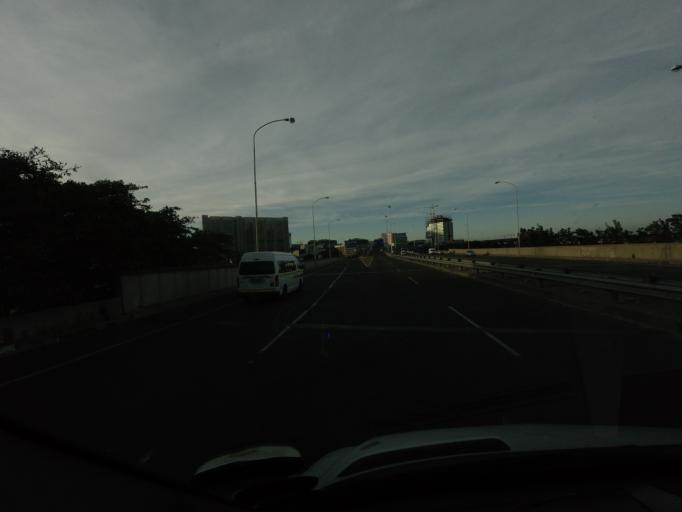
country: ZA
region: Western Cape
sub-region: City of Cape Town
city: Cape Town
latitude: -33.9259
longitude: 18.4332
